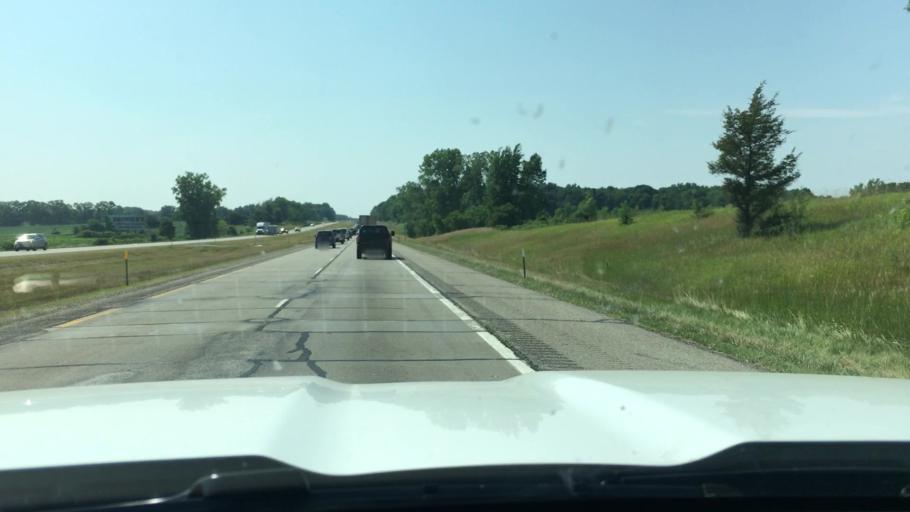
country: US
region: Michigan
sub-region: Eaton County
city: Grand Ledge
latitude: 42.8157
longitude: -84.7969
